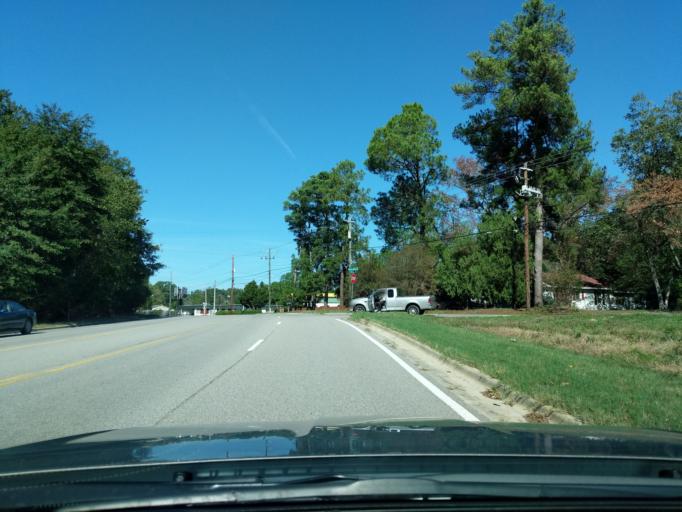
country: US
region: Georgia
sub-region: Richmond County
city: Augusta
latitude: 33.4338
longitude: -82.0088
